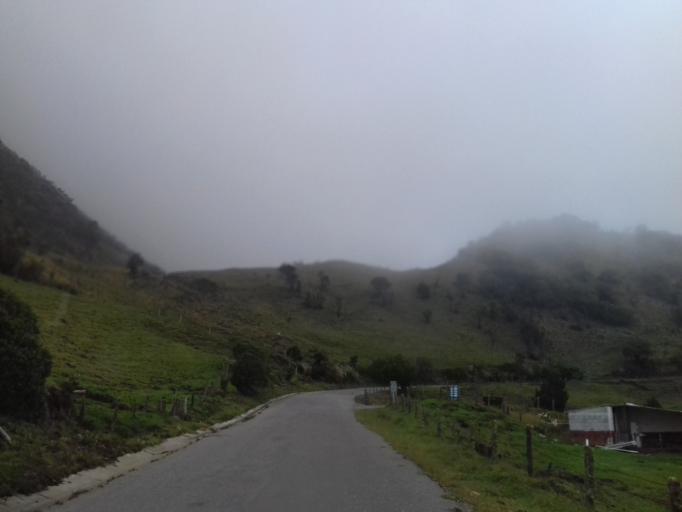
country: CO
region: Caldas
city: Villamaria
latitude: 4.9882
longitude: -75.3330
